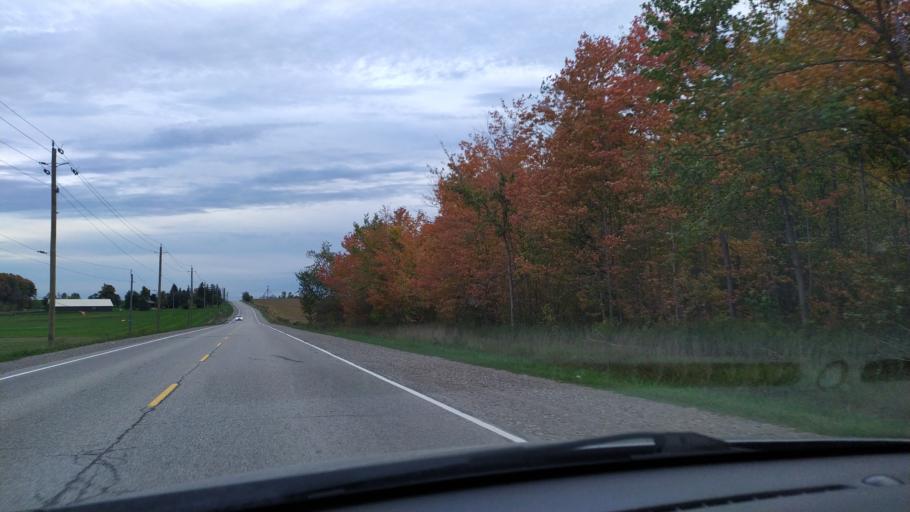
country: CA
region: Ontario
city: Stratford
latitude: 43.5088
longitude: -80.7586
